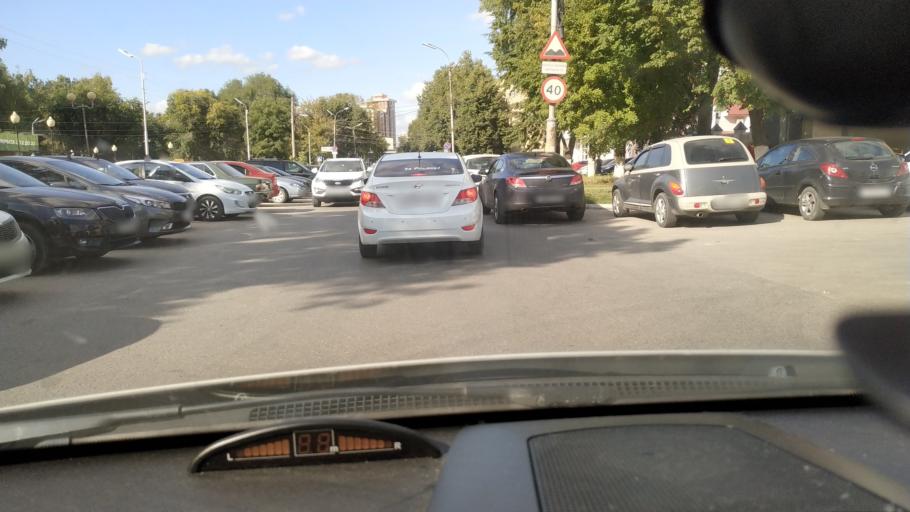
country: RU
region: Rjazan
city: Ryazan'
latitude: 54.6266
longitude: 39.7111
